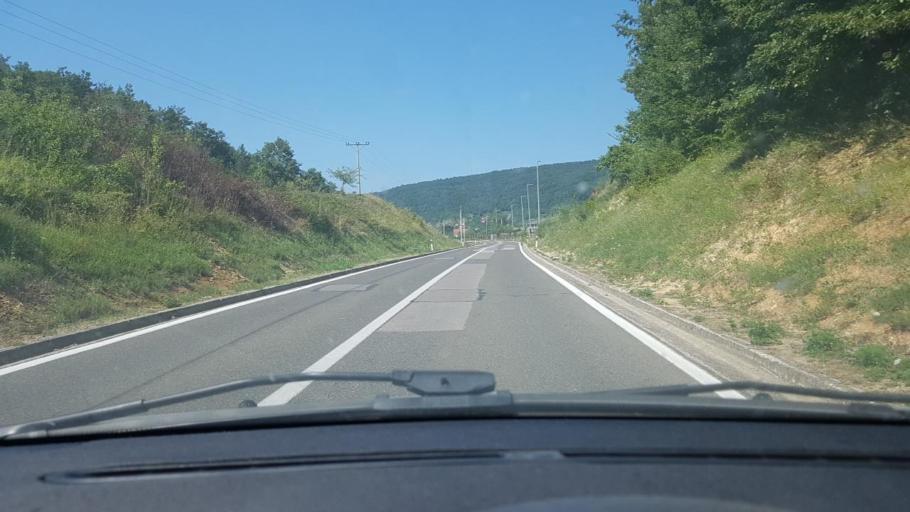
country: BA
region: Federation of Bosnia and Herzegovina
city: Bihac
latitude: 44.7620
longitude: 15.9443
